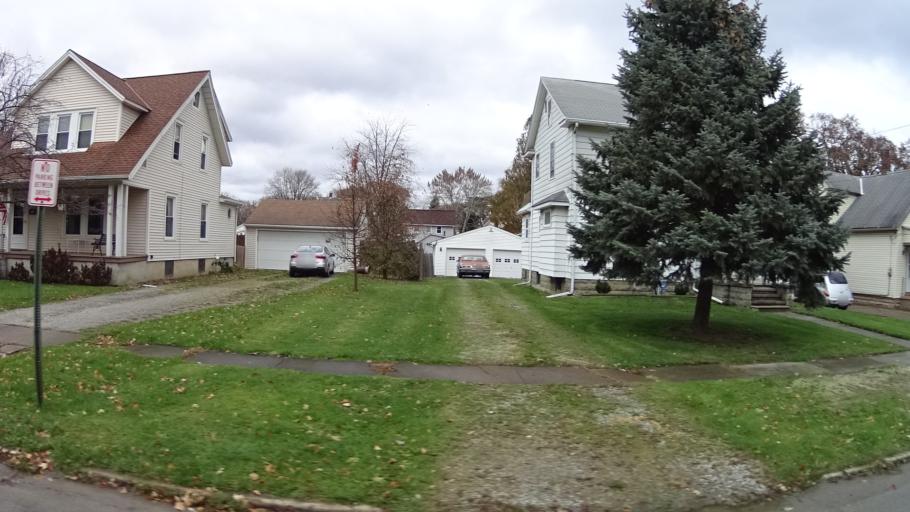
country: US
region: Ohio
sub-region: Lorain County
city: Elyria
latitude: 41.3808
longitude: -82.1264
